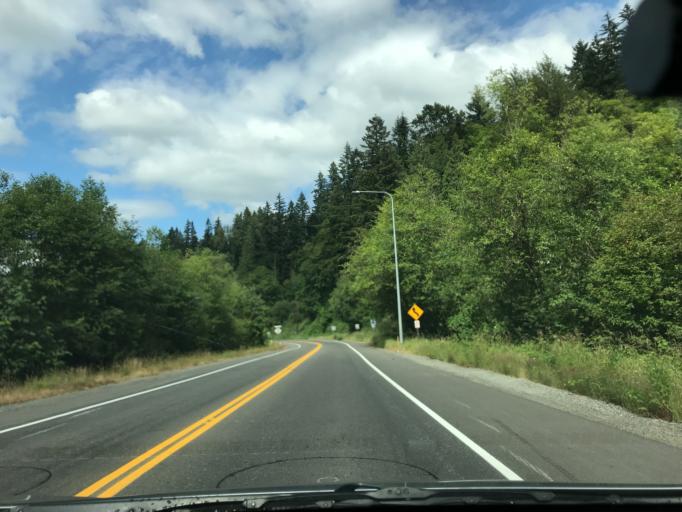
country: US
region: Washington
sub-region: King County
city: Lea Hill
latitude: 47.3024
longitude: -122.1739
